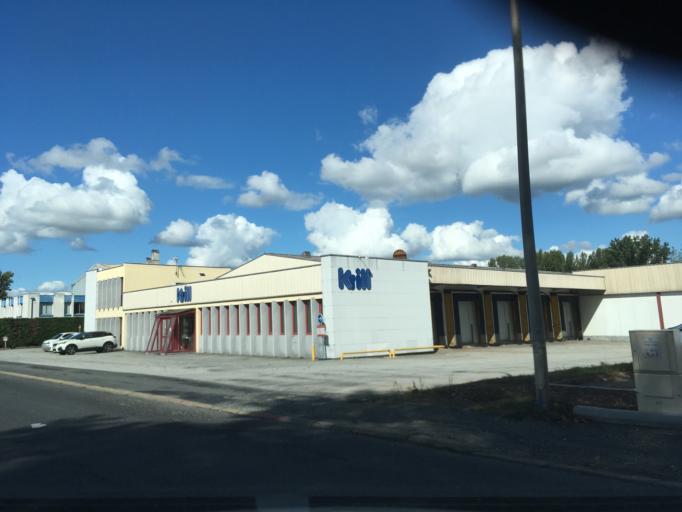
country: FR
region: Limousin
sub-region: Departement de la Correze
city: Saint-Pantaleon-de-Larche
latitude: 45.1499
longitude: 1.4818
